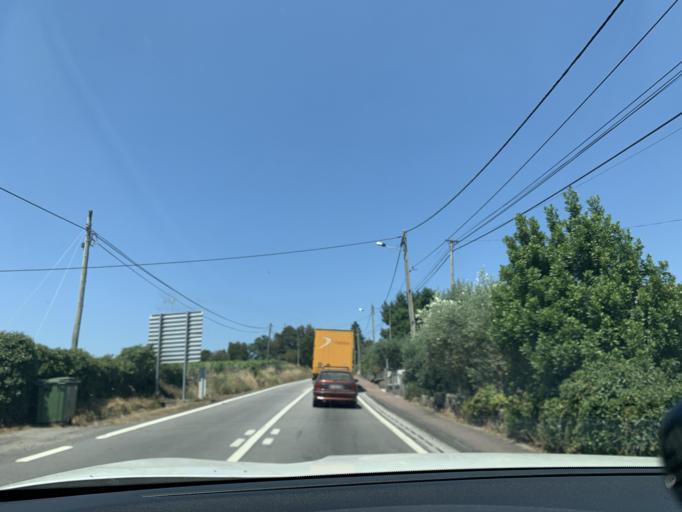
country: PT
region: Viseu
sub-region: Mangualde
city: Mangualde
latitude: 40.5774
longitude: -7.8089
